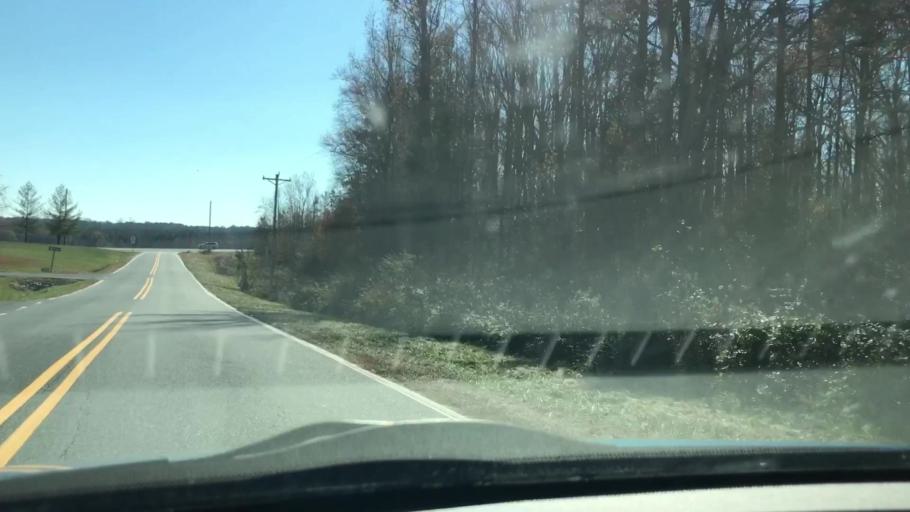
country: US
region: North Carolina
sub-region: Davidson County
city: Denton
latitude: 35.6414
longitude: -79.9725
